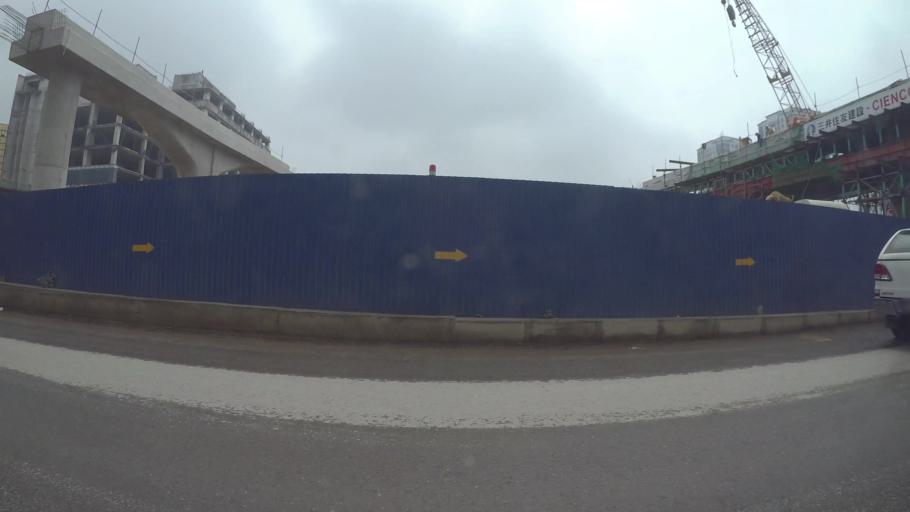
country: VN
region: Ha Noi
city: Cau Dien
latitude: 21.0523
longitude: 105.7814
